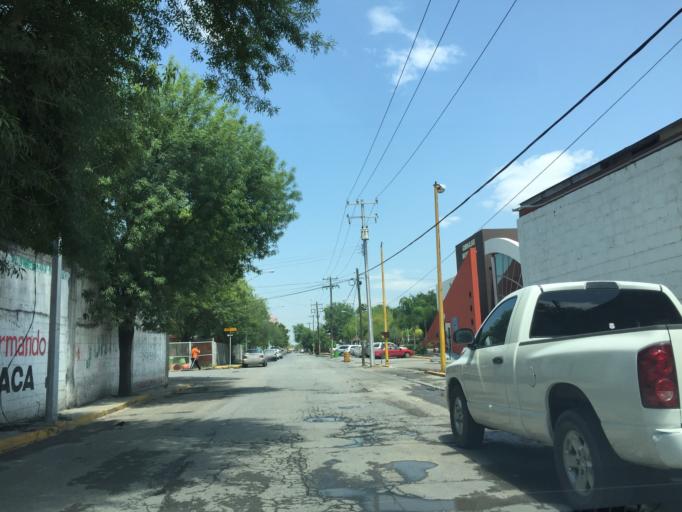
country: MX
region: Nuevo Leon
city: Apodaca
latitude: 25.7823
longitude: -100.1817
